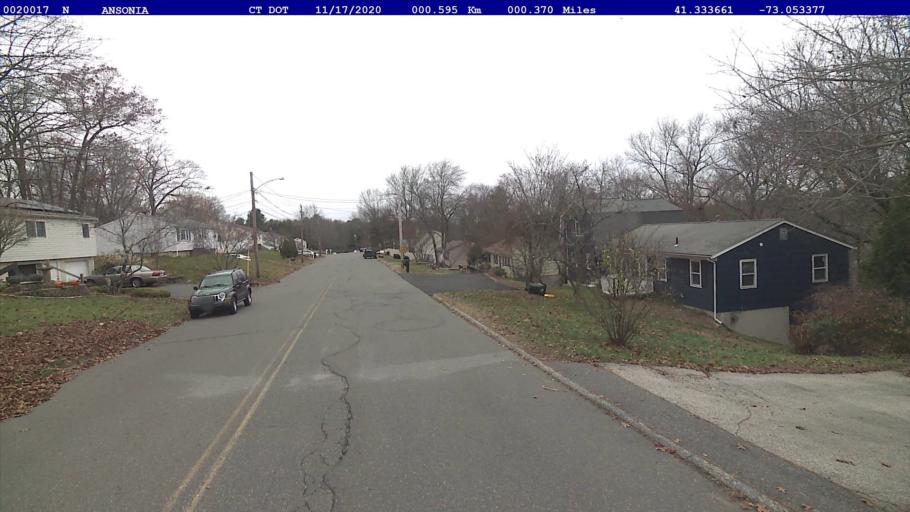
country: US
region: Connecticut
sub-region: New Haven County
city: Ansonia
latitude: 41.3336
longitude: -73.0534
